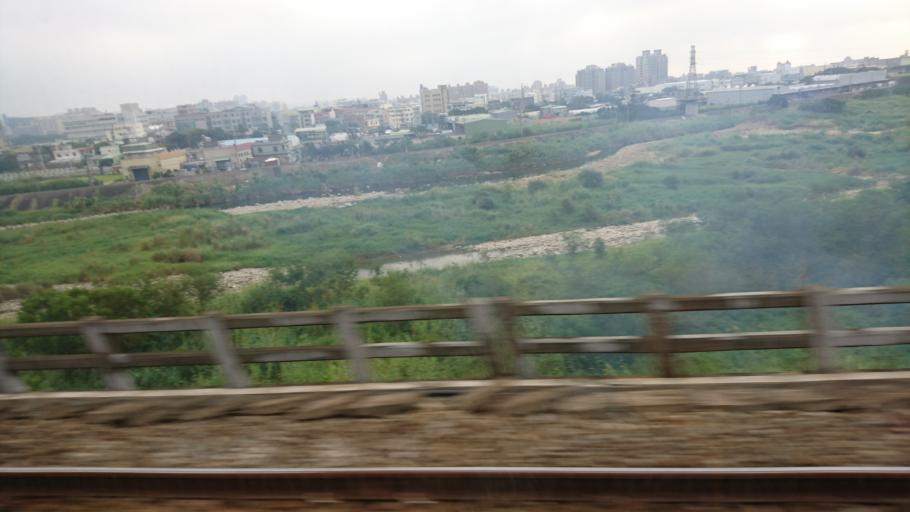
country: TW
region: Taiwan
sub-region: Hsinchu
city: Zhubei
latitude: 24.8536
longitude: 121.0111
